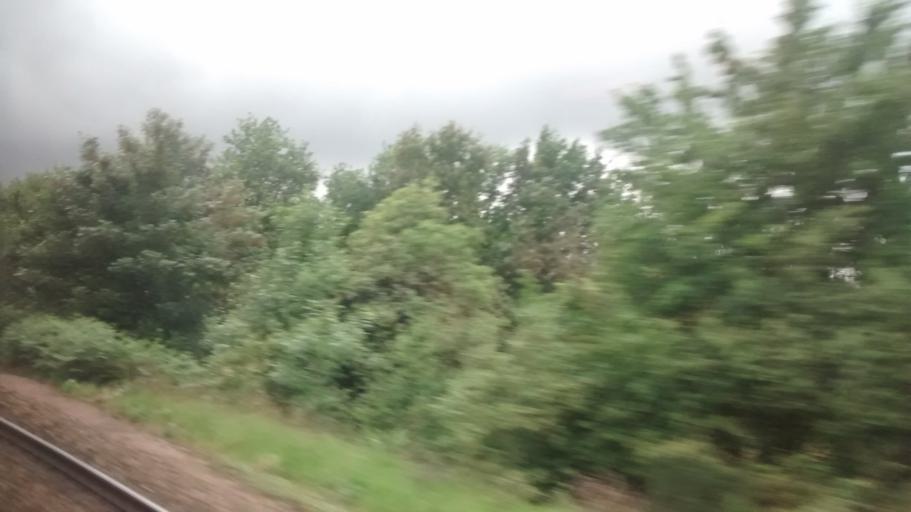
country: FR
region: Pays de la Loire
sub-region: Departement de la Sarthe
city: Change
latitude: 48.0075
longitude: 0.2718
